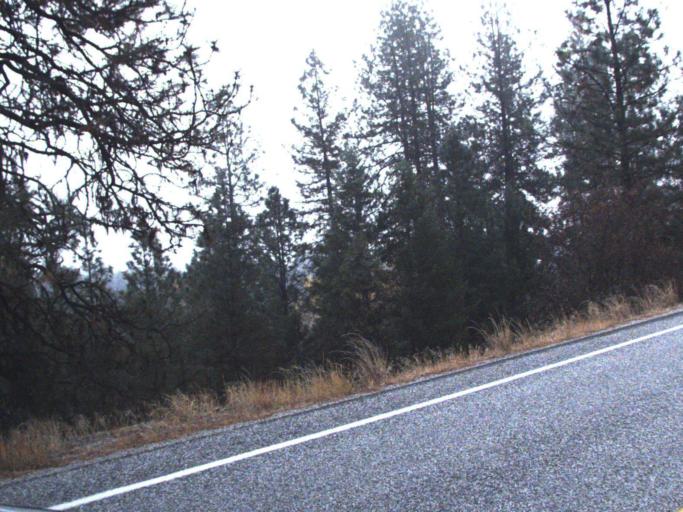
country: CA
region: British Columbia
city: Grand Forks
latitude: 48.8766
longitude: -118.2149
